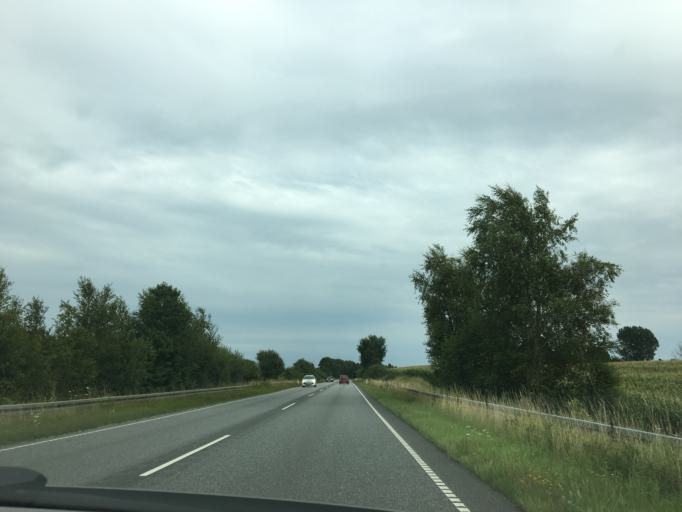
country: DK
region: South Denmark
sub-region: Vejle Kommune
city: Brejning
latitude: 55.6264
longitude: 9.7230
